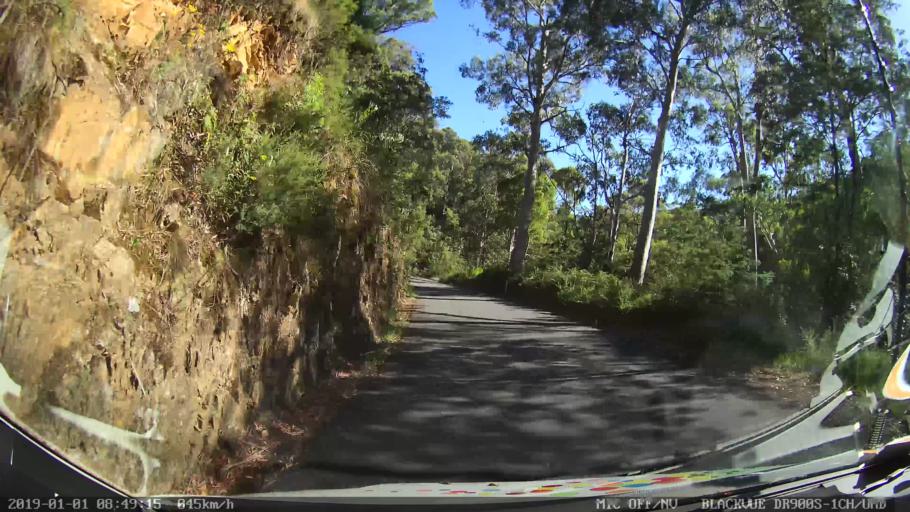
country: AU
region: New South Wales
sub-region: Snowy River
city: Jindabyne
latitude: -36.2836
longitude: 148.1994
